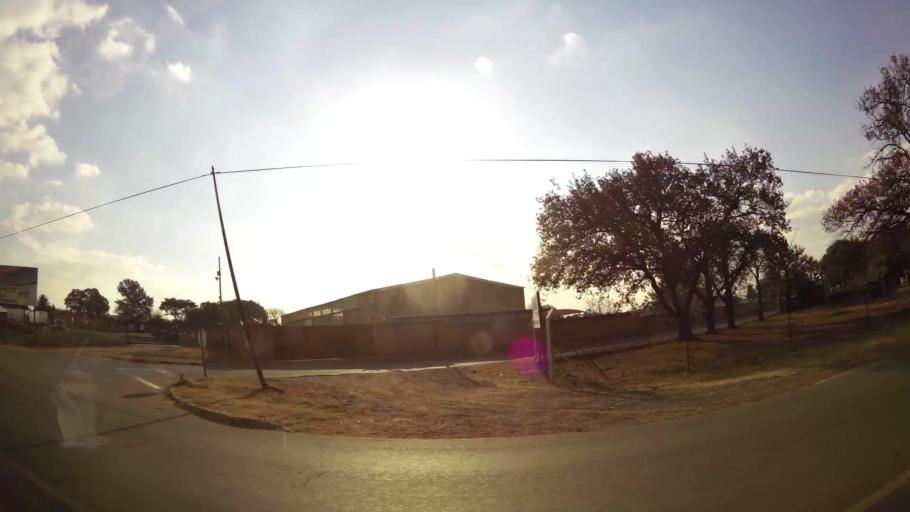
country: ZA
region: Gauteng
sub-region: West Rand District Municipality
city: Krugersdorp
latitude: -26.1008
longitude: 27.7396
